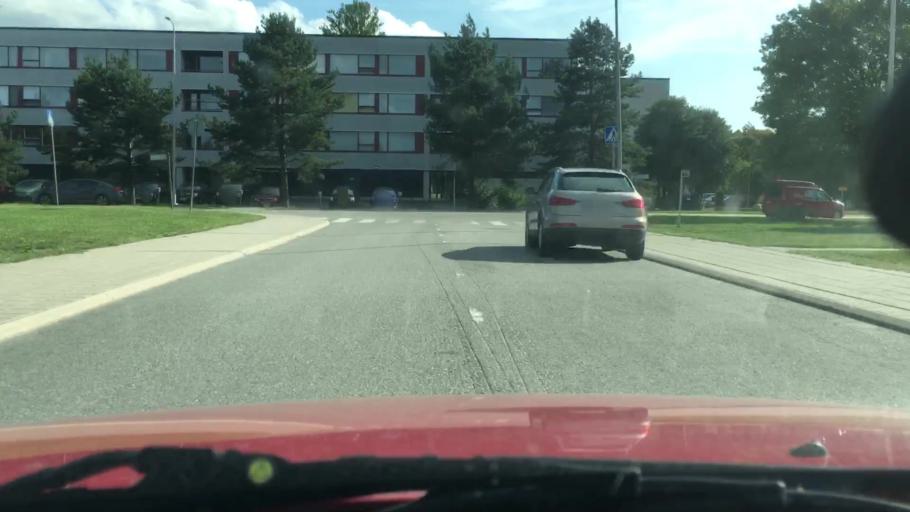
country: FI
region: Varsinais-Suomi
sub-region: Turku
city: Raisio
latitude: 60.4669
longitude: 22.2169
